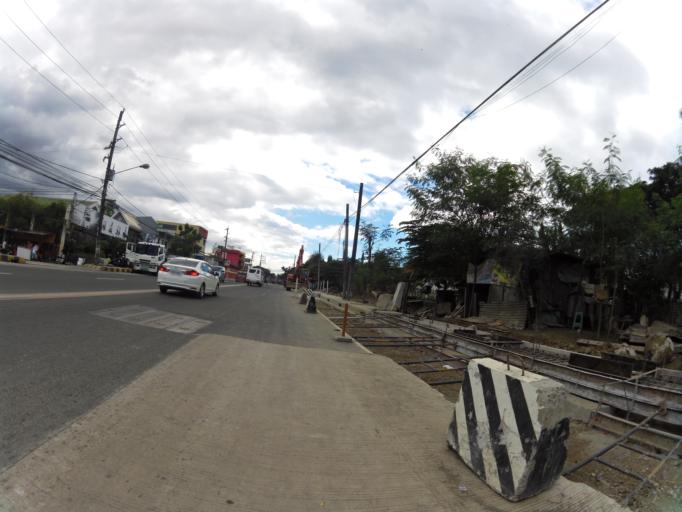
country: PH
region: Calabarzon
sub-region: Province of Rizal
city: Antipolo
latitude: 14.6328
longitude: 121.1129
